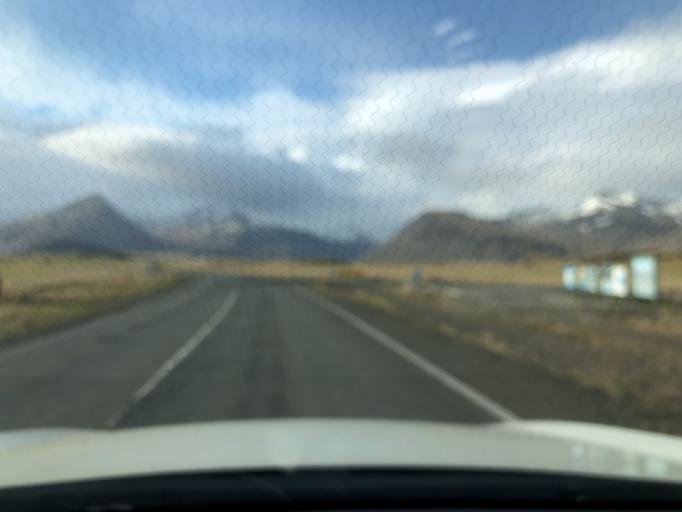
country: IS
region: East
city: Hoefn
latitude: 64.2892
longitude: -15.1824
